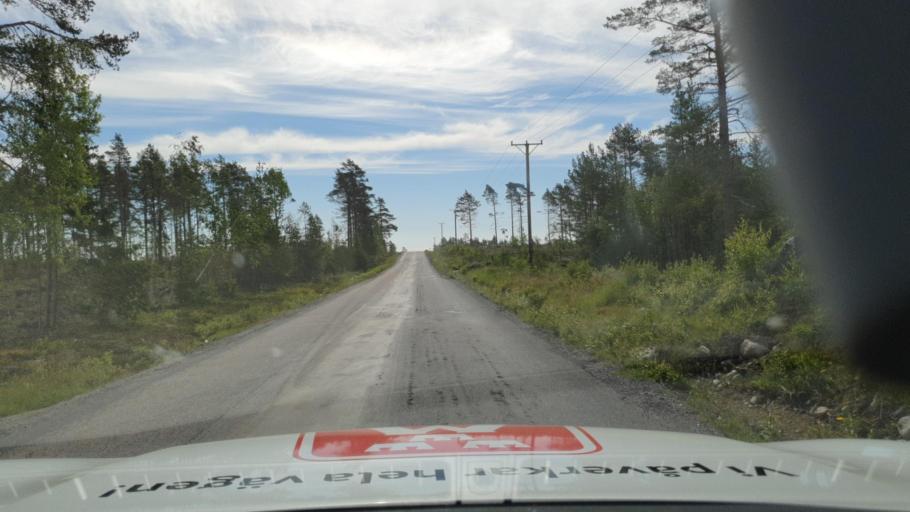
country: SE
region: Vaesterbotten
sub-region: Umea Kommun
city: Saevar
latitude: 63.8745
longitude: 20.7038
